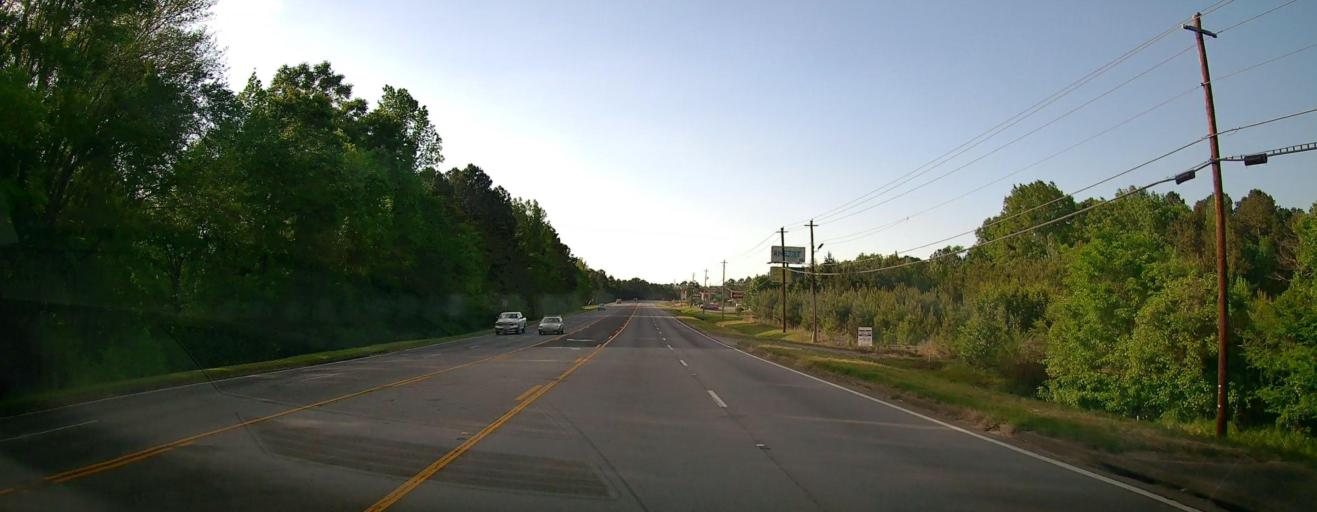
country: US
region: Georgia
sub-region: Baldwin County
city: Milledgeville
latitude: 33.1290
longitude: -83.2672
